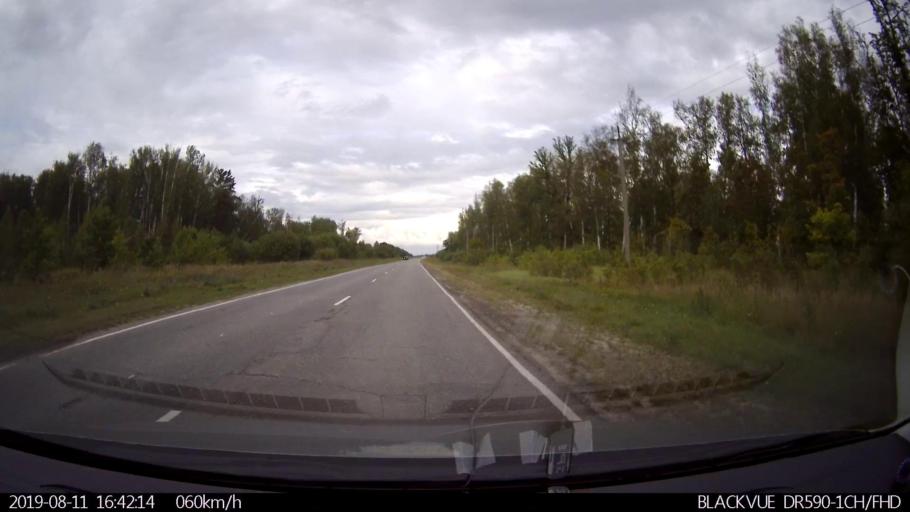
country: RU
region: Ulyanovsk
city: Mayna
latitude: 54.1589
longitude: 47.6605
